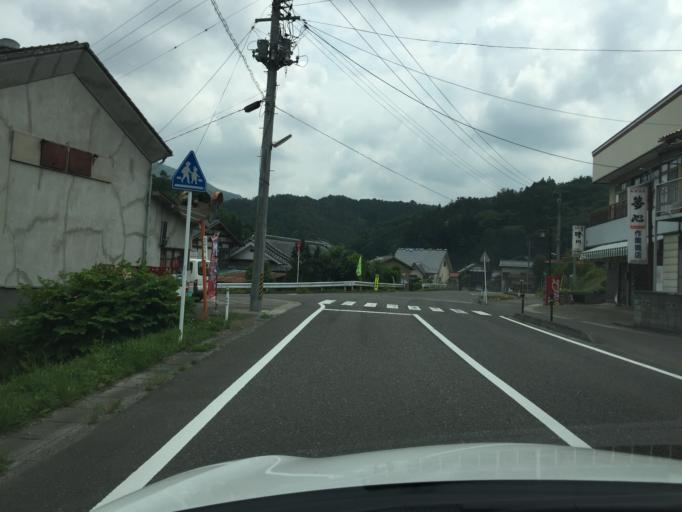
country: JP
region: Fukushima
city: Miharu
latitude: 37.2937
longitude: 140.5386
